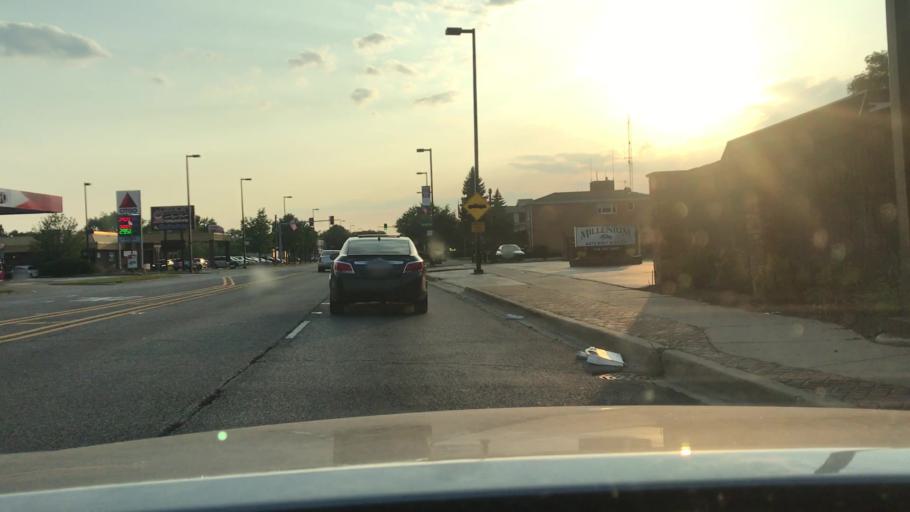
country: US
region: Illinois
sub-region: Cook County
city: Burbank
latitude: 41.7485
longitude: -87.7817
